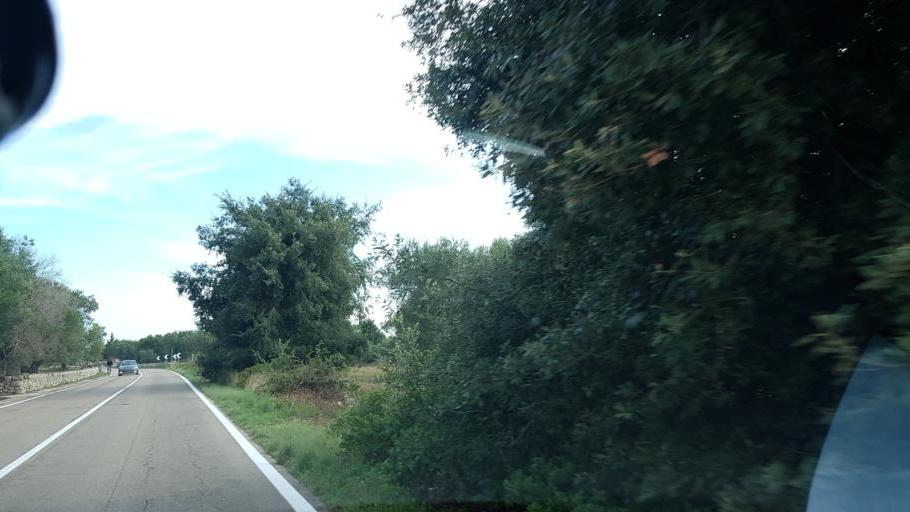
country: IT
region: Apulia
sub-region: Provincia di Lecce
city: Melendugno
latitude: 40.3307
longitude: 18.3437
